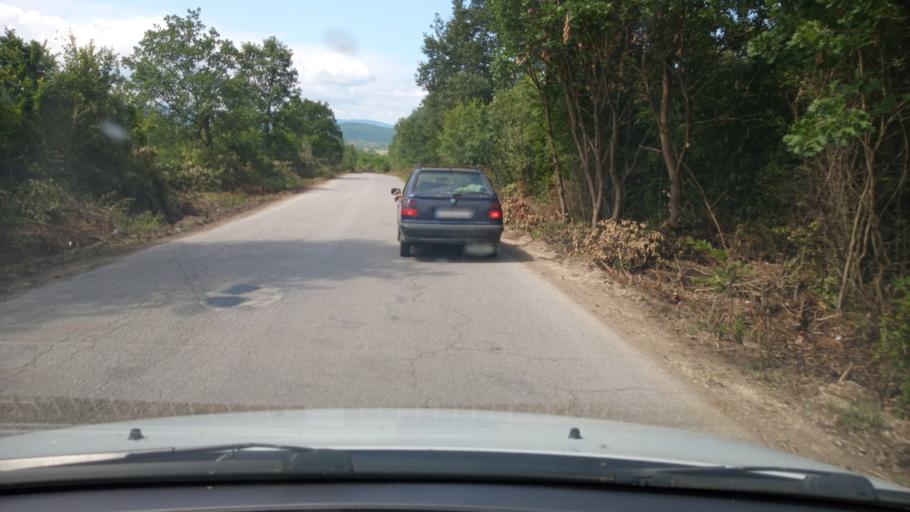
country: BG
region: Lovech
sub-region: Obshtina Lukovit
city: Lukovit
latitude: 43.1915
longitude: 24.0962
